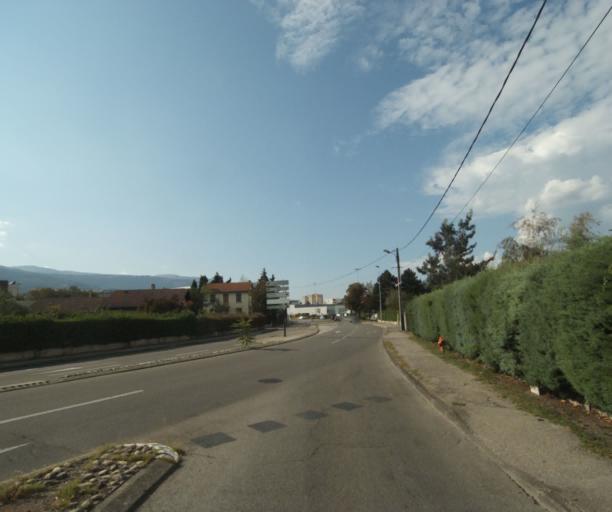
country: FR
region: Rhone-Alpes
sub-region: Departement de l'Isere
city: Echirolles
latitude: 45.1465
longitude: 5.7266
